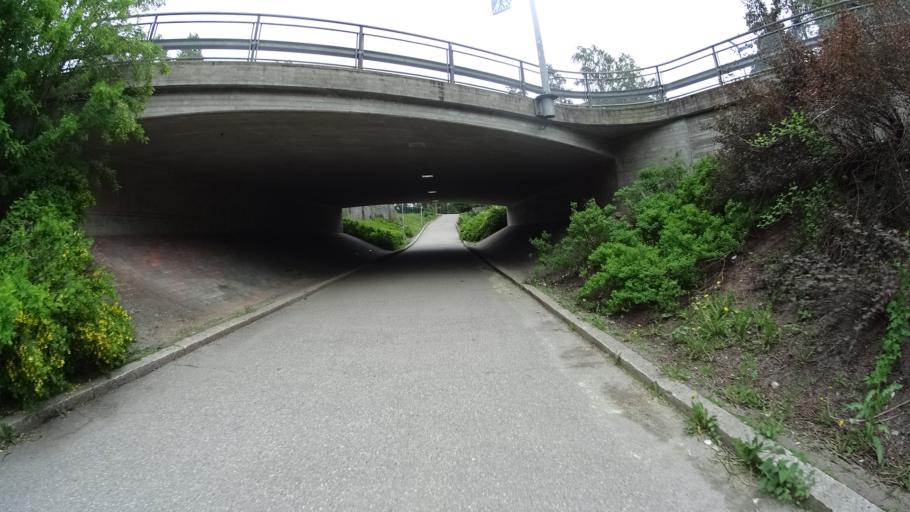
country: FI
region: Uusimaa
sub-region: Helsinki
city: Vantaa
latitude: 60.2424
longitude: 25.0748
